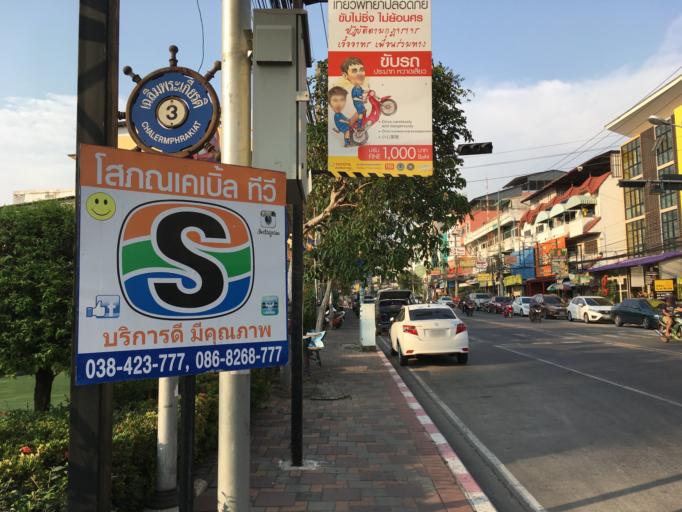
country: TH
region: Chon Buri
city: Phatthaya
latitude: 12.9461
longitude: 100.8961
